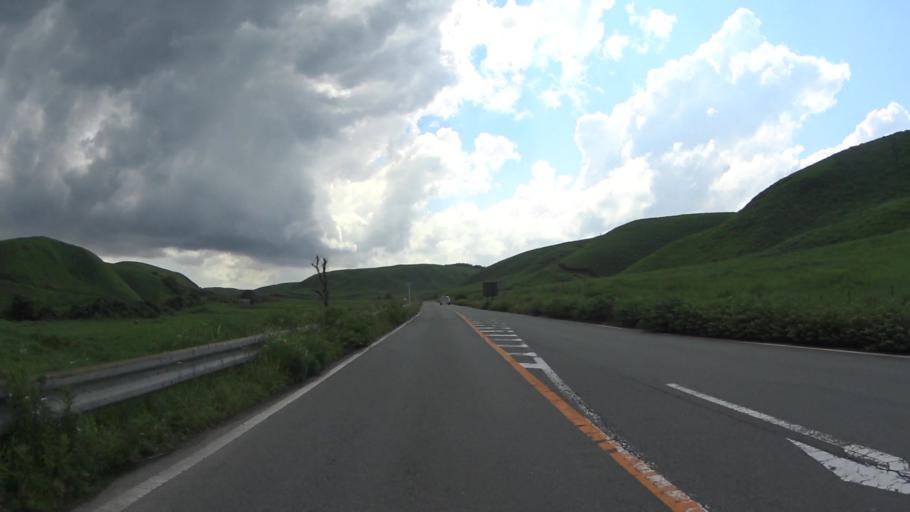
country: JP
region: Kumamoto
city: Aso
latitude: 33.0120
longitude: 131.1522
